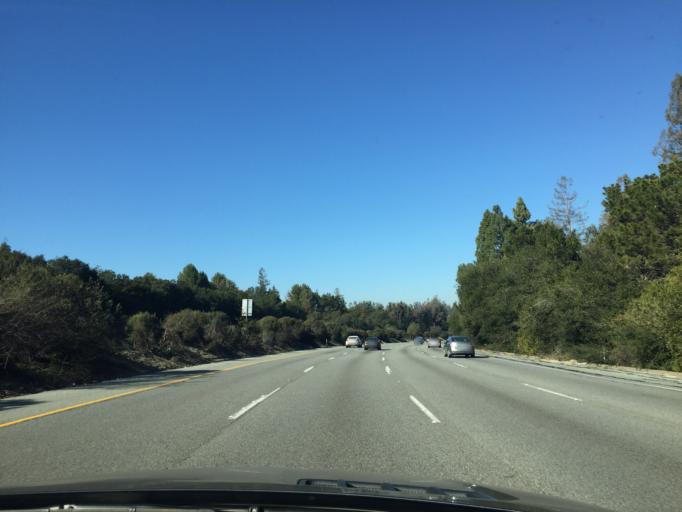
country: US
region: California
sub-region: Santa Clara County
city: Loyola
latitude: 37.3480
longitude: -122.1023
